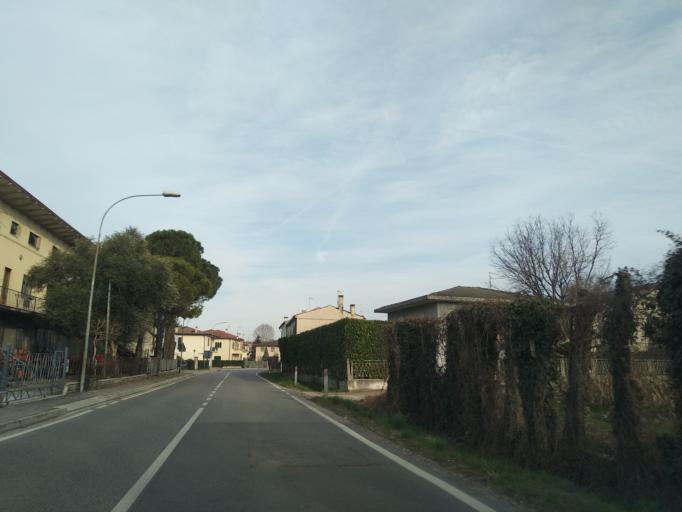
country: IT
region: Veneto
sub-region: Provincia di Vicenza
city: Ponte di Barbarano
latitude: 45.3925
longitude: 11.5716
